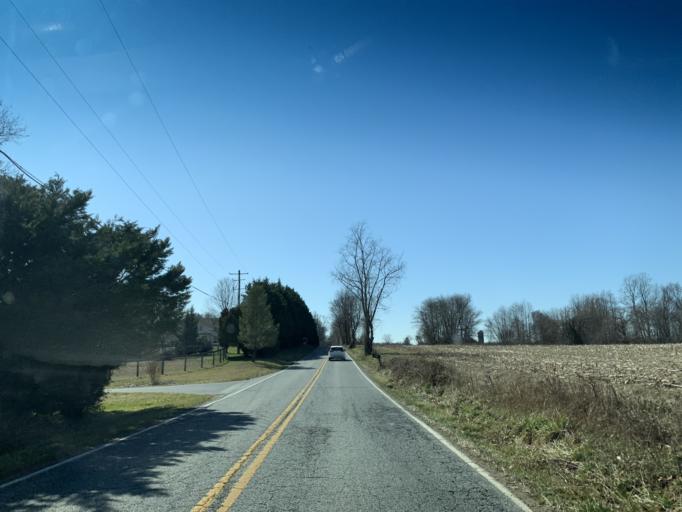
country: US
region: Maryland
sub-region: Cecil County
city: Charlestown
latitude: 39.4593
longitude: -75.8909
